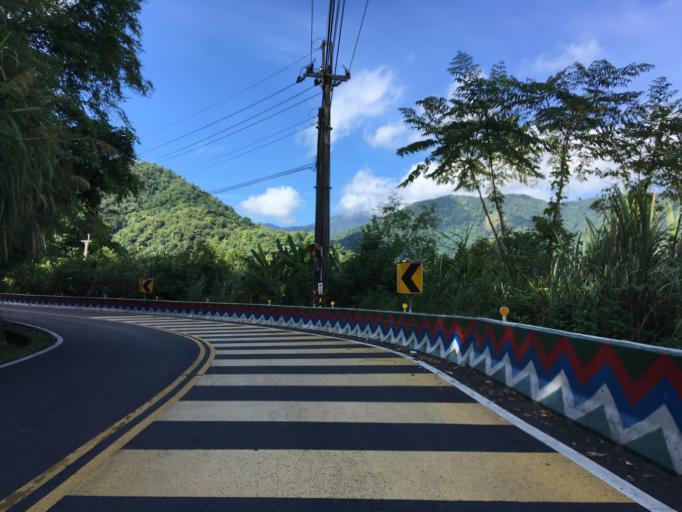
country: TW
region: Taiwan
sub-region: Yilan
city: Yilan
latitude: 24.6134
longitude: 121.6909
